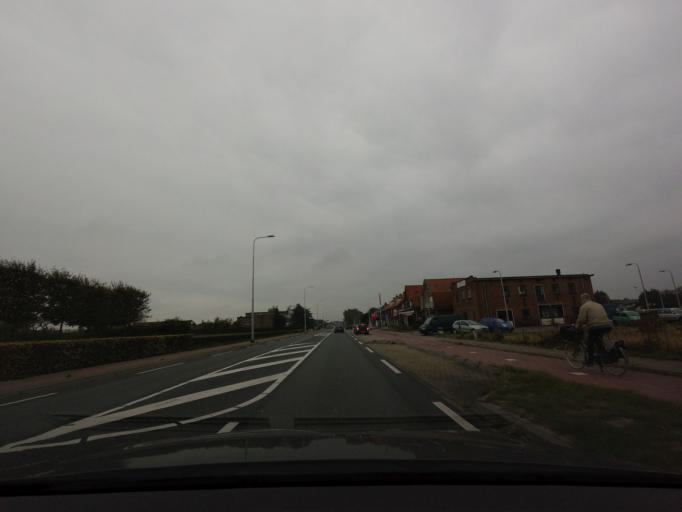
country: NL
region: South Holland
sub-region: Gemeente Teylingen
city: Sassenheim
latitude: 52.2402
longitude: 4.5372
